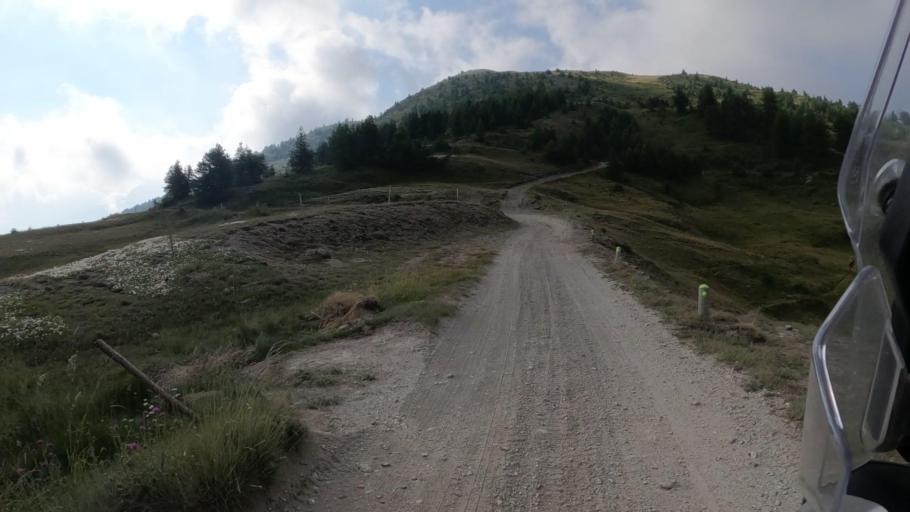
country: IT
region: Piedmont
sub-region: Provincia di Torino
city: Sauze d'Oulx
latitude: 45.0216
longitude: 6.8995
